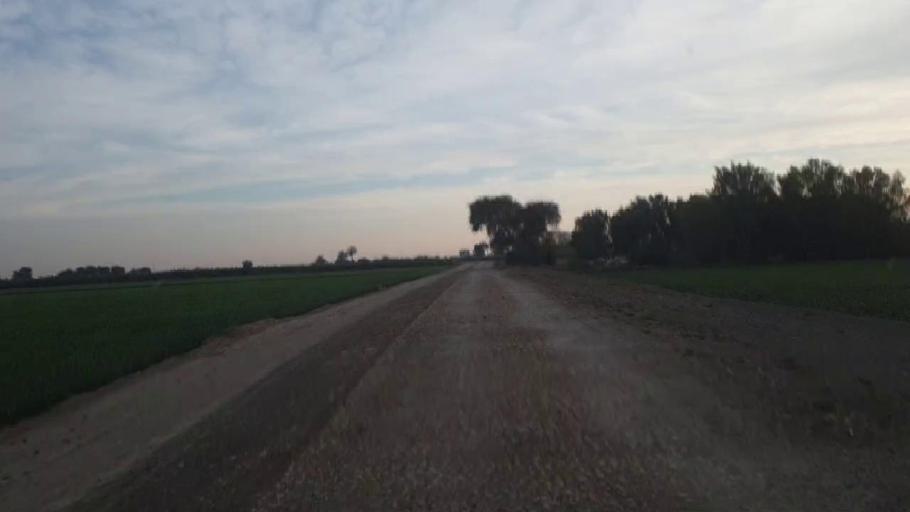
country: PK
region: Sindh
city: Shahdadpur
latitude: 26.0524
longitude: 68.5323
